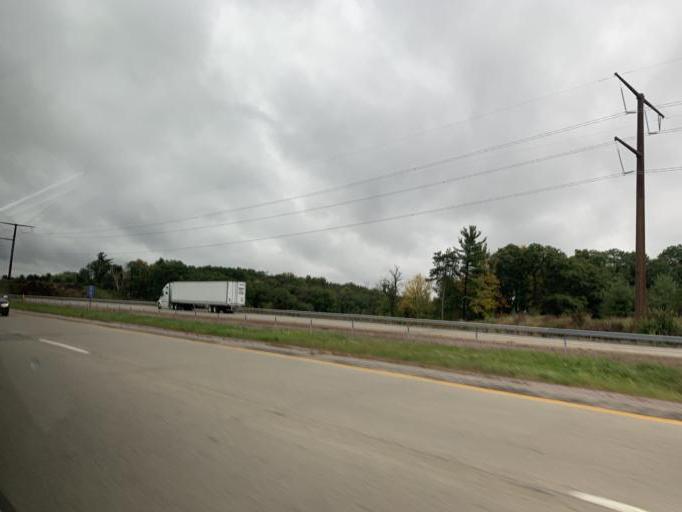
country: US
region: Wisconsin
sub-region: Sauk County
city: Lake Delton
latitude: 43.6184
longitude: -89.8049
